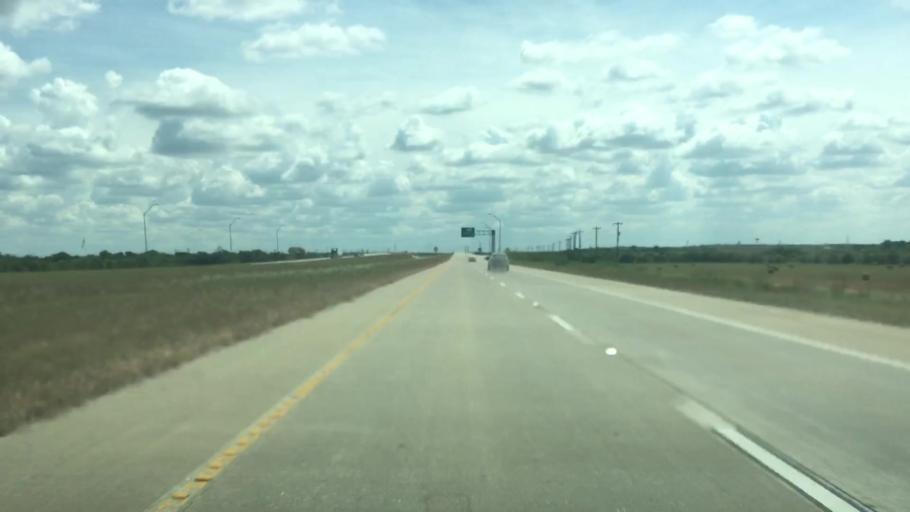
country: US
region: Texas
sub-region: Travis County
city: Onion Creek
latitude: 30.0869
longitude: -97.7427
